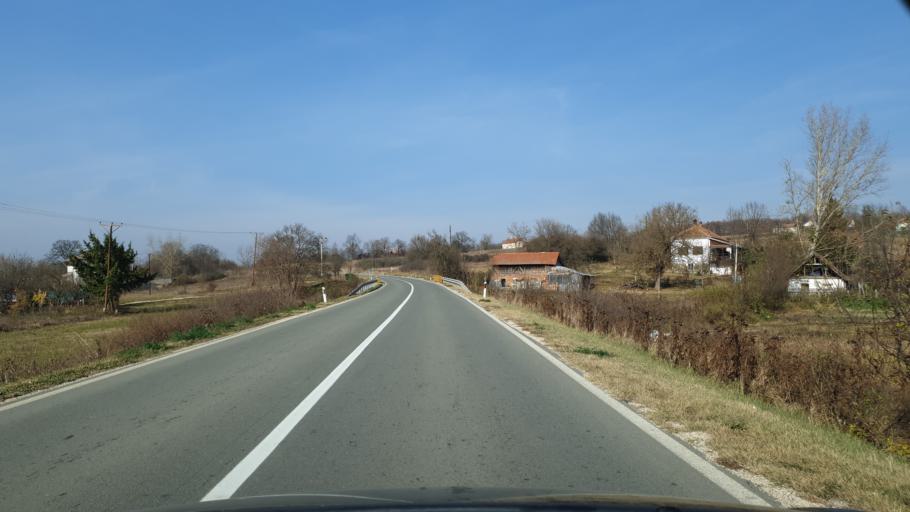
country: RS
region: Central Serbia
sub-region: Borski Okrug
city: Bor
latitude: 43.9299
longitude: 22.0936
